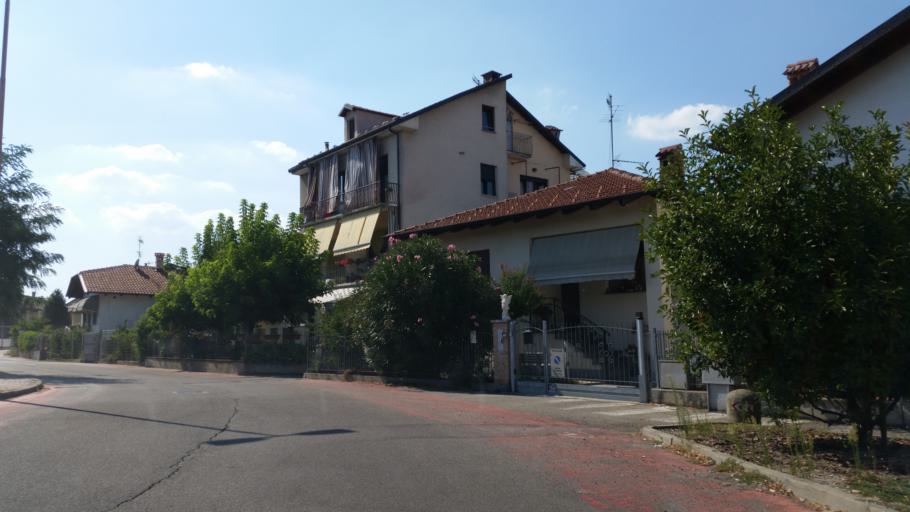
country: IT
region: Piedmont
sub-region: Provincia di Cuneo
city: Alba
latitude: 44.6997
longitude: 8.0203
